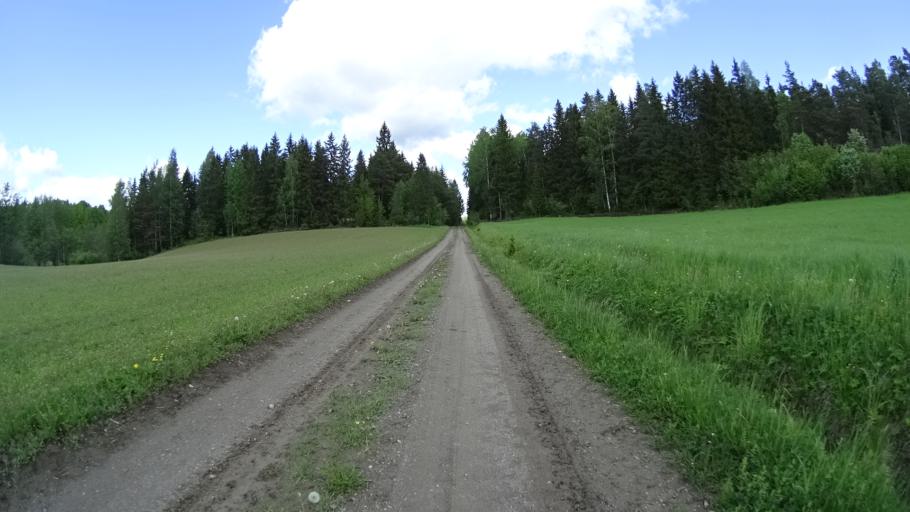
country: FI
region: Uusimaa
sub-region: Raaseporin
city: Karis
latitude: 60.1480
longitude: 23.6224
